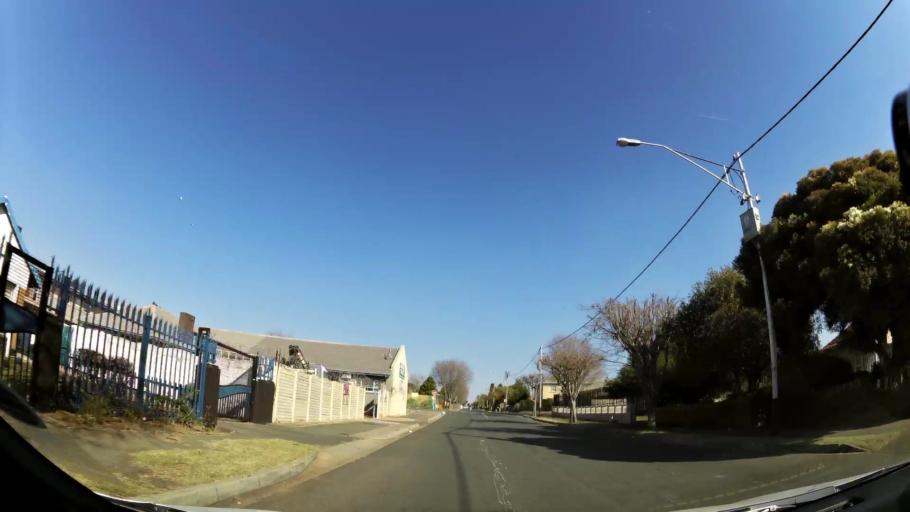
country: ZA
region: Gauteng
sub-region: City of Johannesburg Metropolitan Municipality
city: Johannesburg
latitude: -26.2471
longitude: 28.0079
